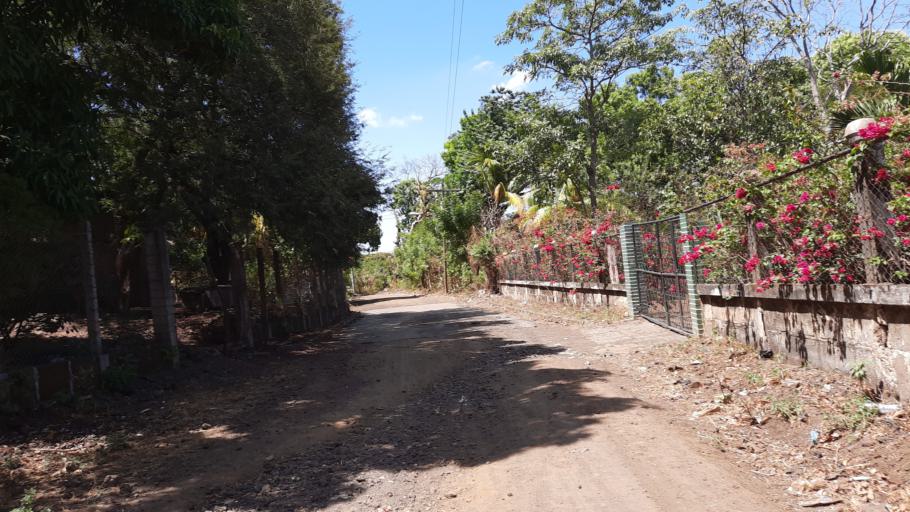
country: NI
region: Masaya
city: Ticuantepe
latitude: 12.0316
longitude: -86.1667
